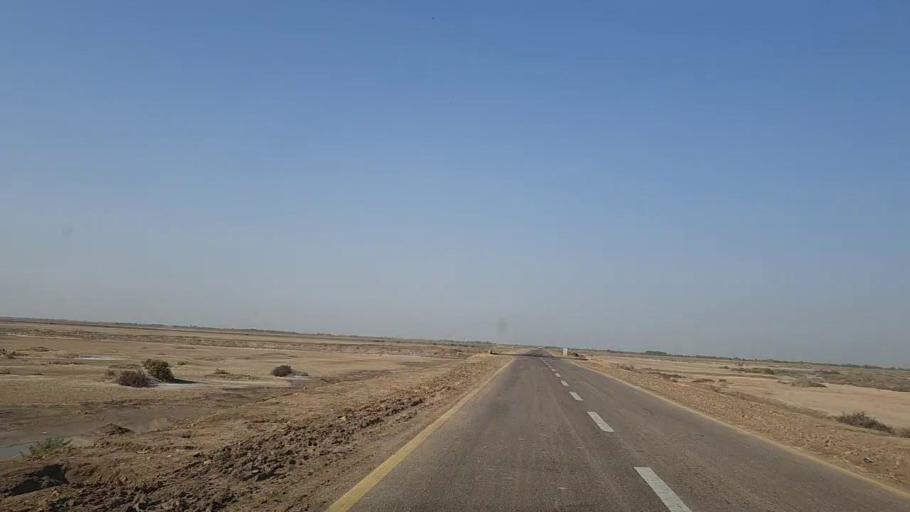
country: PK
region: Sindh
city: Jati
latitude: 24.4935
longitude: 68.3758
